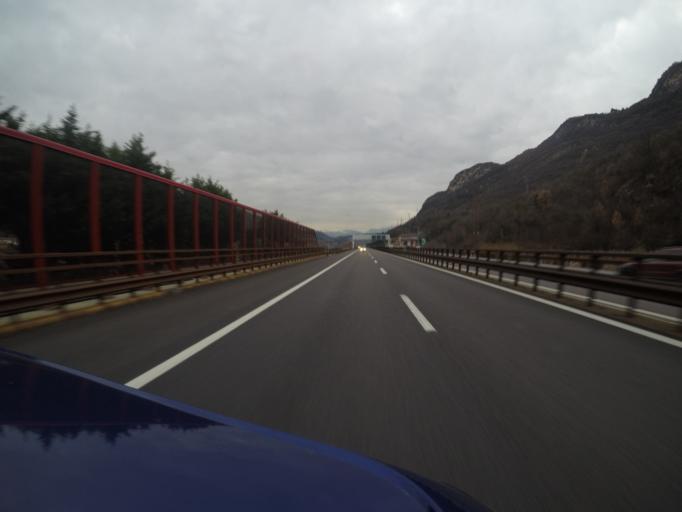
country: IT
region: Trentino-Alto Adige
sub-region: Provincia di Trento
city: Calliano
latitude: 45.9405
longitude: 11.0937
